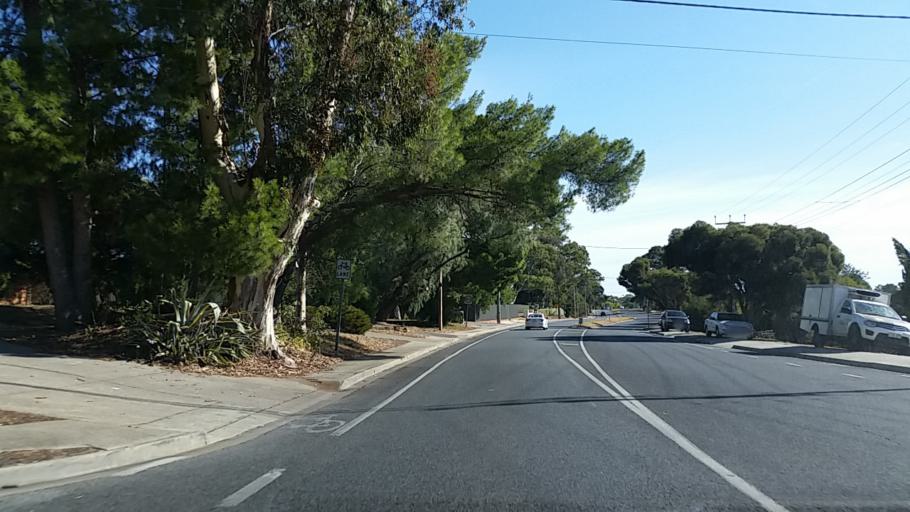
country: AU
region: South Australia
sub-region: Tea Tree Gully
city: Hope Valley
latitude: -34.8495
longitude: 138.7151
